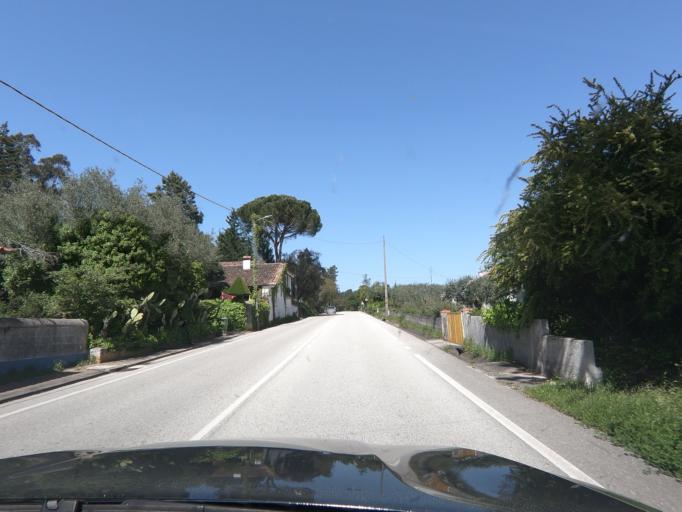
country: PT
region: Coimbra
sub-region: Vila Nova de Poiares
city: Poiares
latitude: 40.1856
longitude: -8.2581
